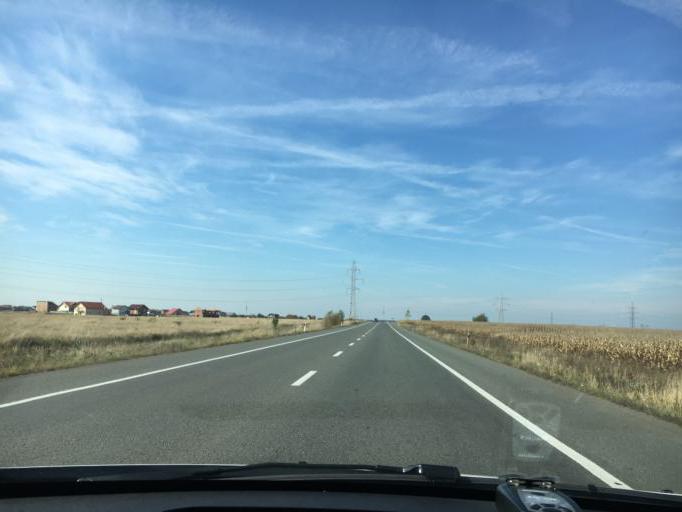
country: RO
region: Timis
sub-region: Comuna Dumbravita
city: Dumbravita
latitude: 45.8138
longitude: 21.2537
